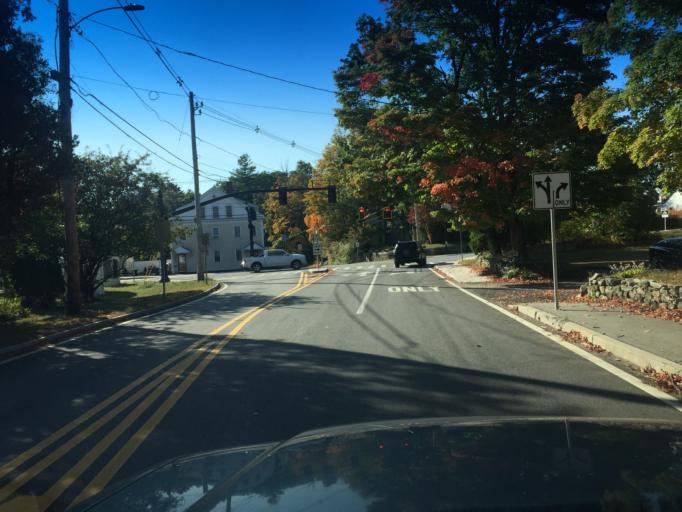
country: US
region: Massachusetts
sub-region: Norfolk County
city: Medway
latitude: 42.1484
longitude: -71.4252
